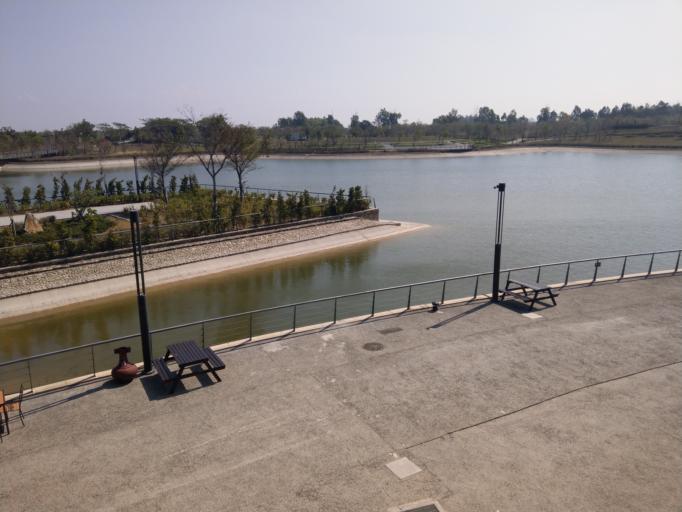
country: TW
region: Taiwan
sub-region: Chiayi
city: Taibao
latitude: 23.4725
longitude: 120.2929
